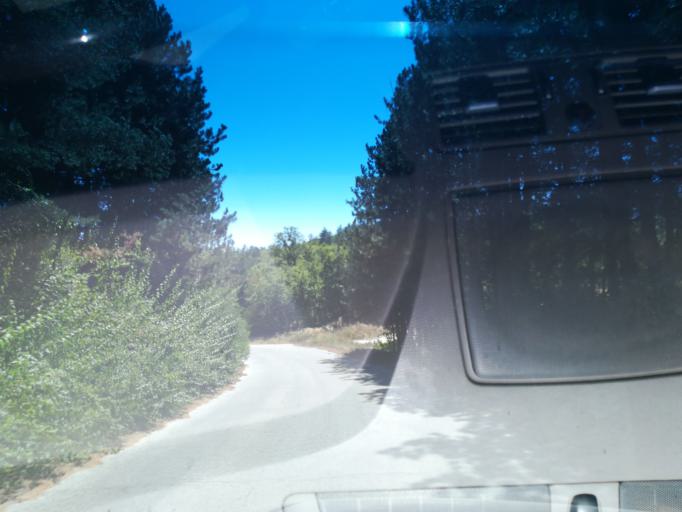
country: BG
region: Pazardzhik
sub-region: Obshtina Strelcha
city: Strelcha
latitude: 42.5432
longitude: 24.3302
